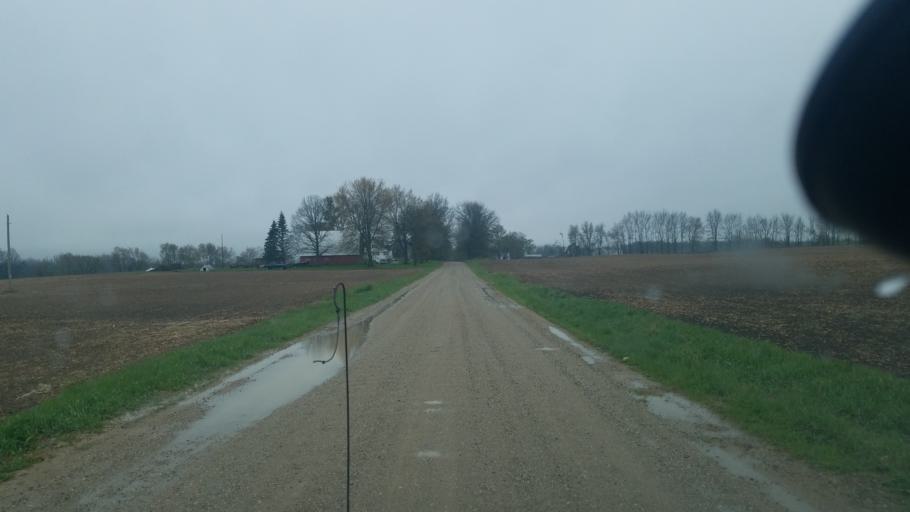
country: US
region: Michigan
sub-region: Montcalm County
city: Lakeview
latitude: 43.4748
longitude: -85.3332
